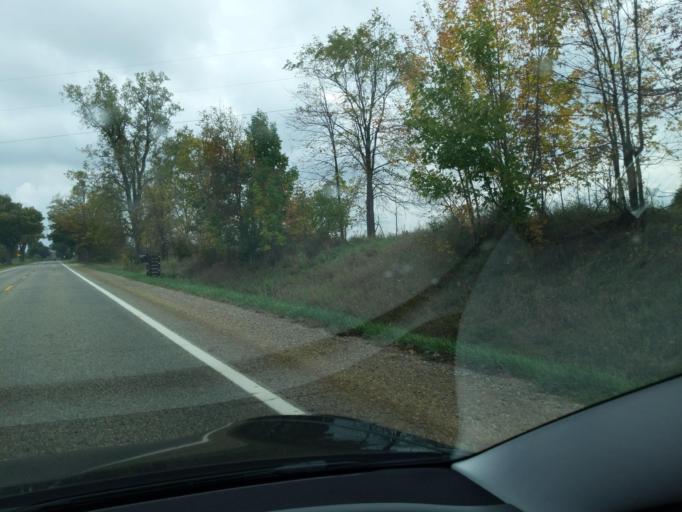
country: US
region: Michigan
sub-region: Eaton County
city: Potterville
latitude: 42.5476
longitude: -84.7483
